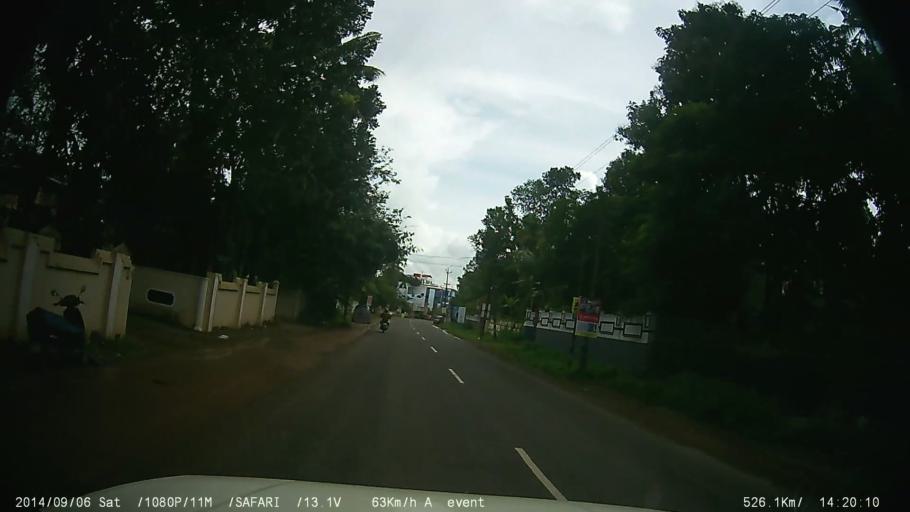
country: IN
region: Kerala
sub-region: Kottayam
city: Kottayam
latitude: 9.6540
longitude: 76.5511
